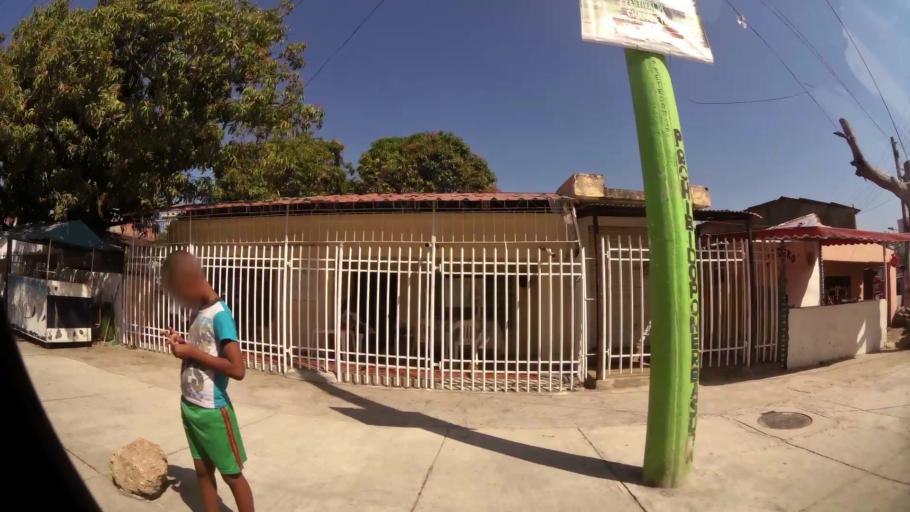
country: CO
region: Bolivar
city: Cartagena
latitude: 10.3788
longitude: -75.4716
